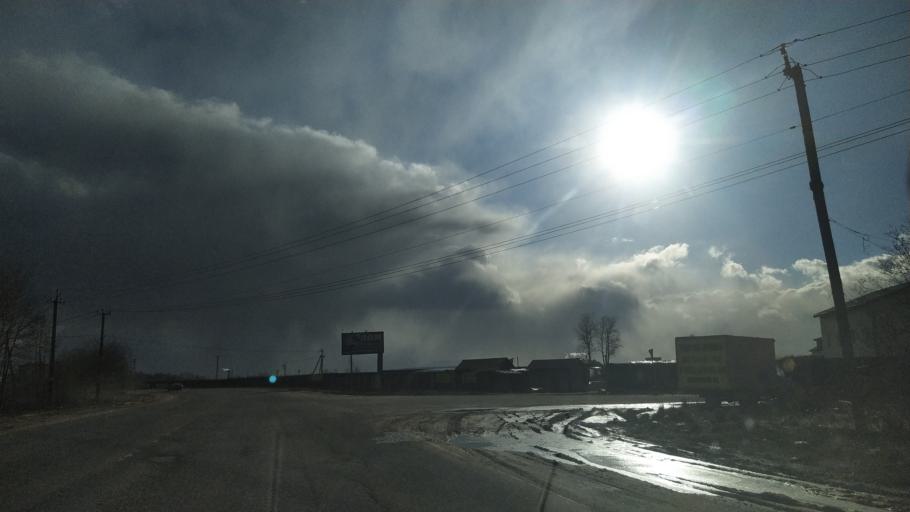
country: RU
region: Leningrad
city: Bugry
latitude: 60.0850
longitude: 30.3938
